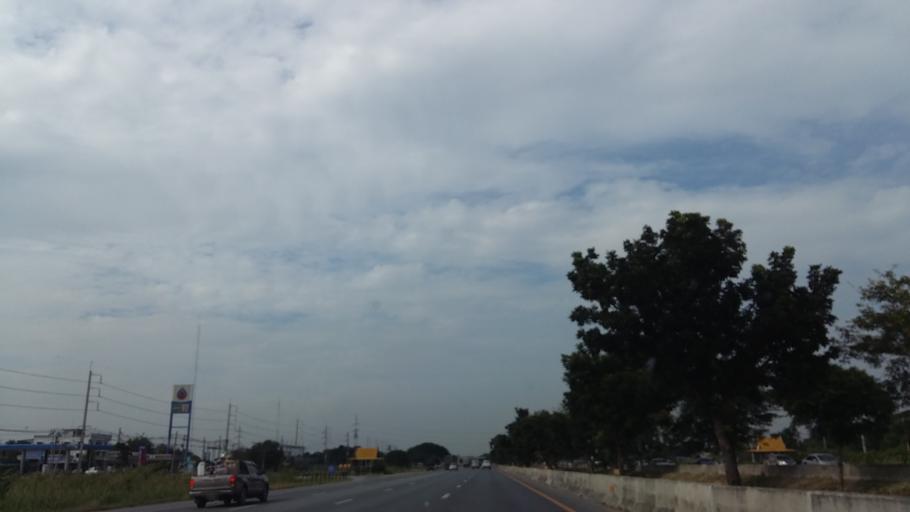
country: TH
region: Phra Nakhon Si Ayutthaya
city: Maha Rat
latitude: 14.5008
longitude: 100.5215
